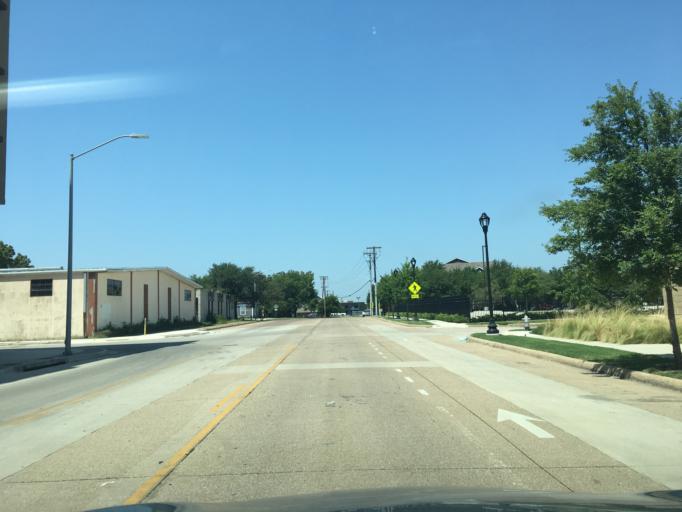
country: US
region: Texas
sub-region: Tarrant County
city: Fort Worth
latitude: 32.7380
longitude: -97.3269
